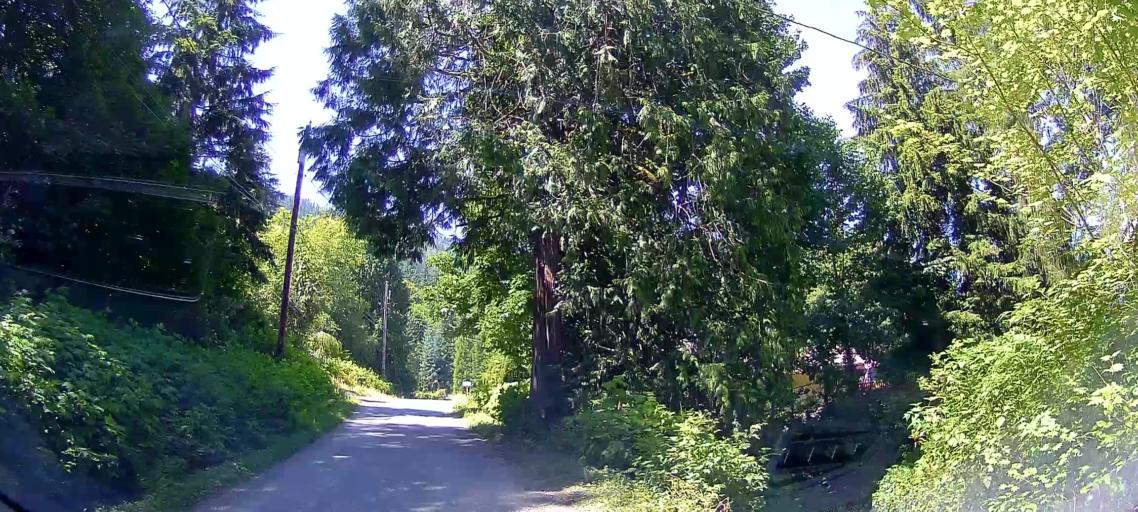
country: US
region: Washington
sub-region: Whatcom County
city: Sudden Valley
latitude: 48.6474
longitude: -122.3306
